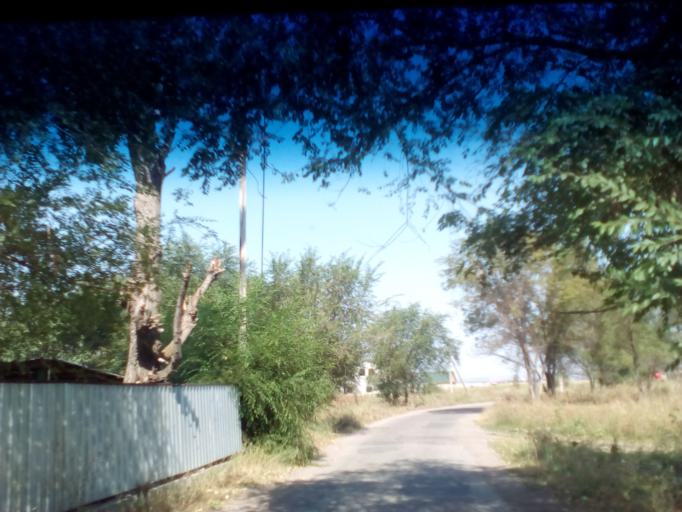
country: KZ
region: Almaty Oblysy
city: Burunday
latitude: 43.1634
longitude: 76.3865
